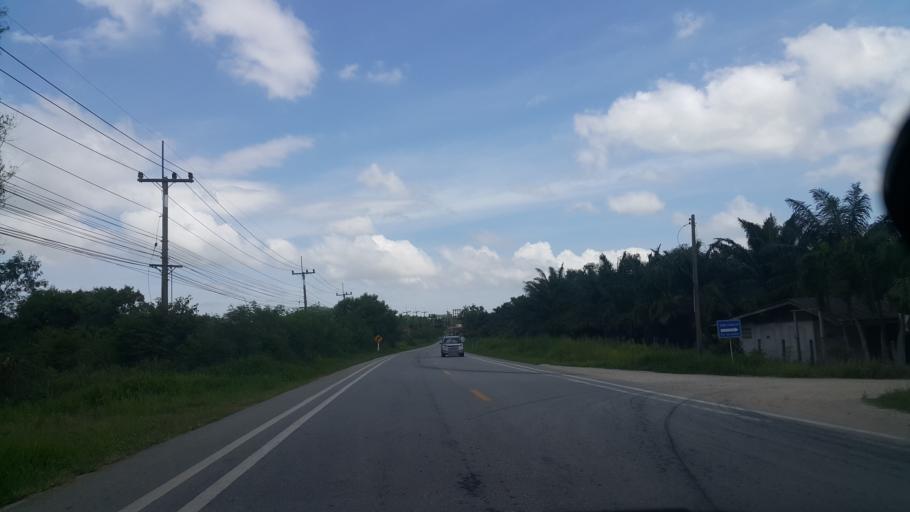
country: TH
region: Rayong
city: Ban Chang
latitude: 12.8147
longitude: 101.0595
